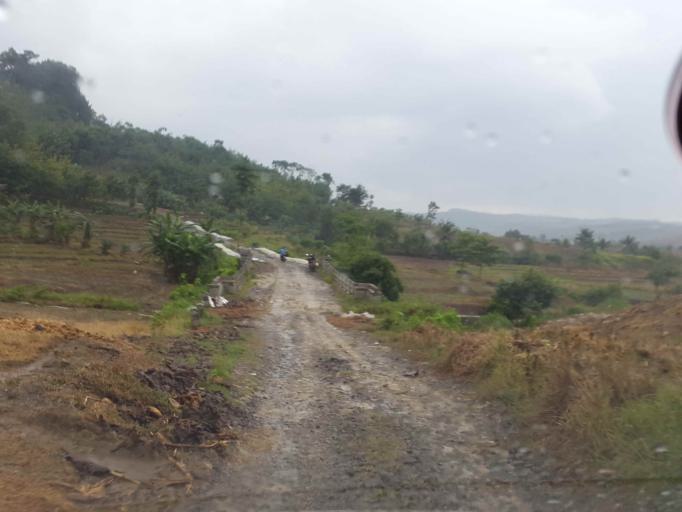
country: ID
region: Central Java
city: Kadumanis
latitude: -7.1398
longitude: 108.9039
